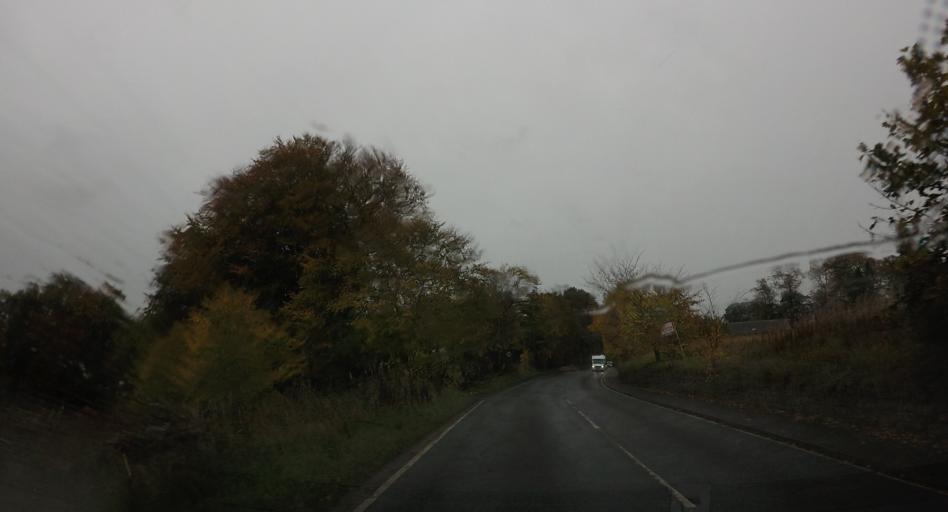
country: GB
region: Scotland
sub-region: Perth and Kinross
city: Coupar Angus
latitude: 56.5497
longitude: -3.2723
